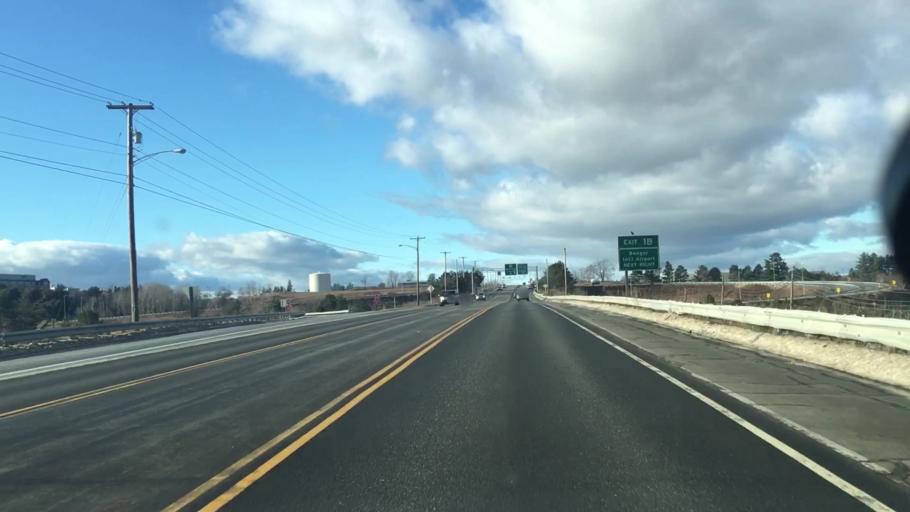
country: US
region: Maine
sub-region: Penobscot County
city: Holden
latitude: 44.7699
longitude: -68.7182
